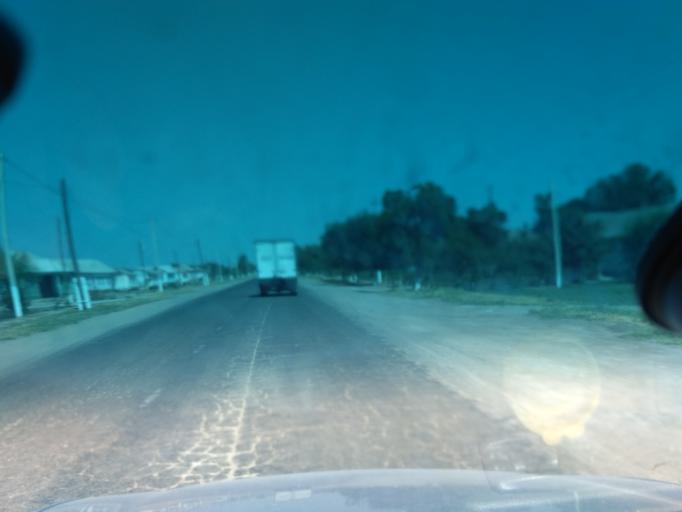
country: UZ
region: Sirdaryo
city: Guliston
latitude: 40.4877
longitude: 68.8808
